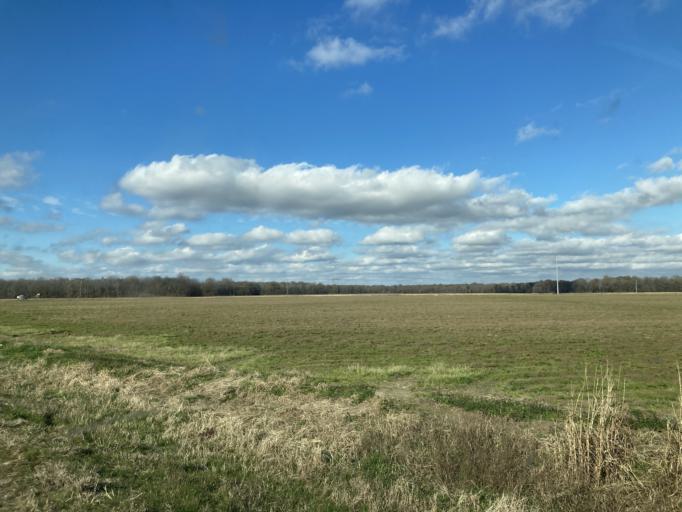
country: US
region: Mississippi
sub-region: Yazoo County
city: Yazoo City
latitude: 32.9596
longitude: -90.4873
